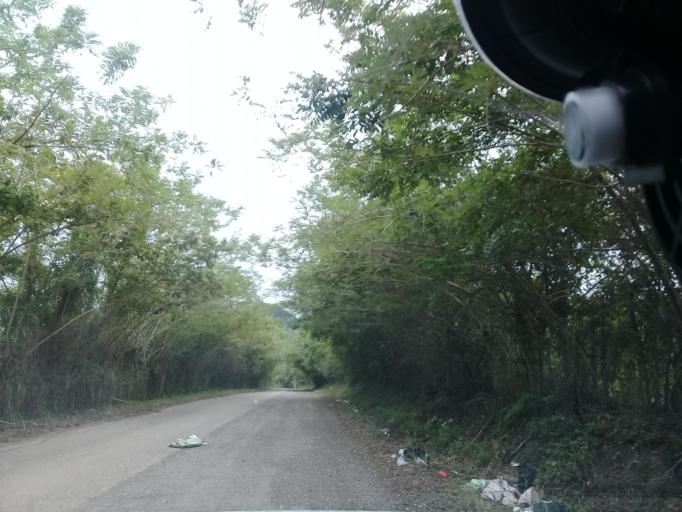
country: MX
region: Veracruz
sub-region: Chalma
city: San Pedro Coyutla
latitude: 21.2111
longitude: -98.3852
